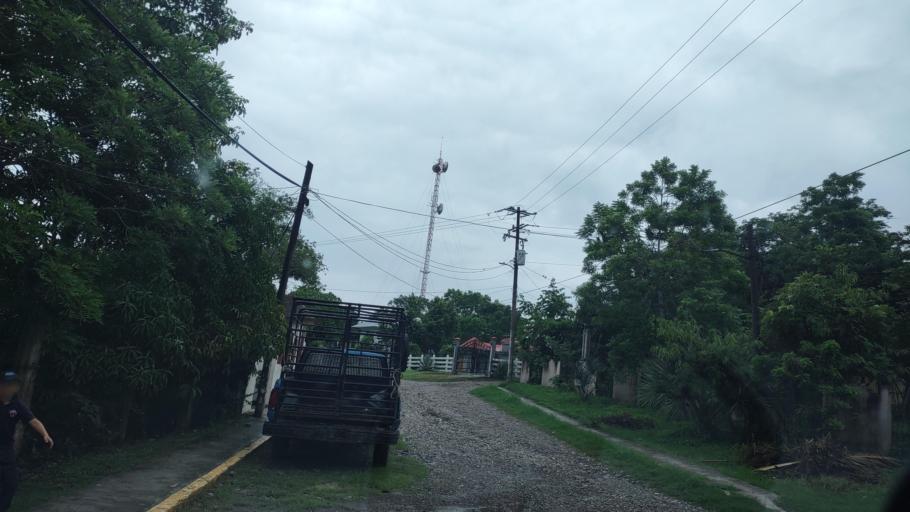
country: MX
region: San Luis Potosi
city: Tanquian de Escobedo
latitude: 21.5444
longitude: -98.5516
